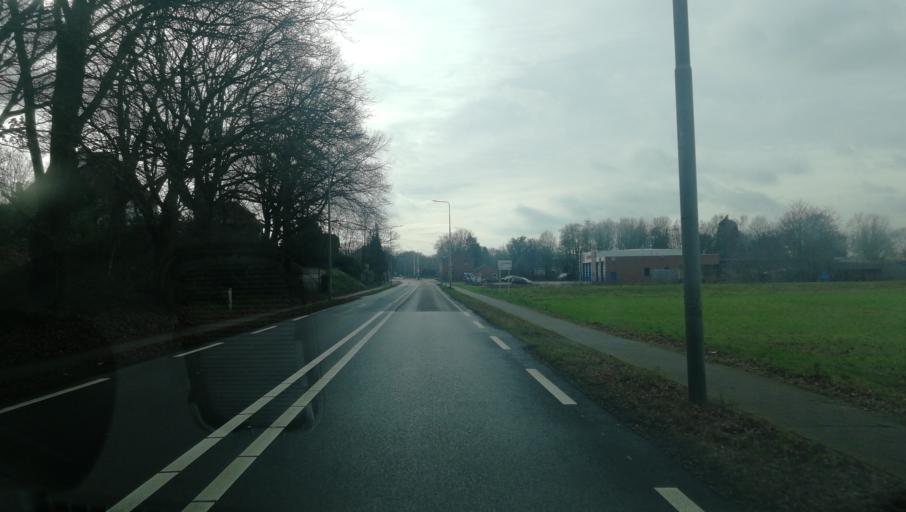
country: NL
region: Limburg
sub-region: Gemeente Beesel
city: Offenbeek
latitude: 51.3144
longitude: 6.1116
